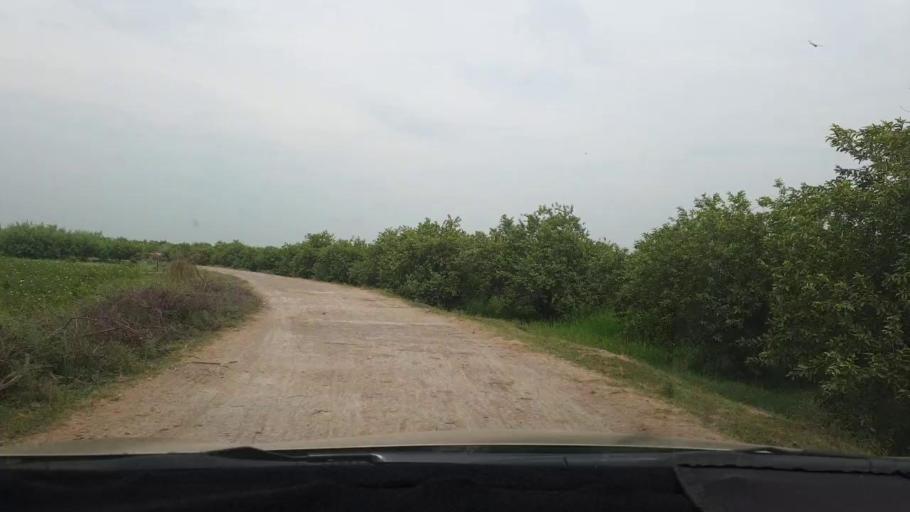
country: PK
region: Sindh
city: Naudero
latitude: 27.6341
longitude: 68.3433
